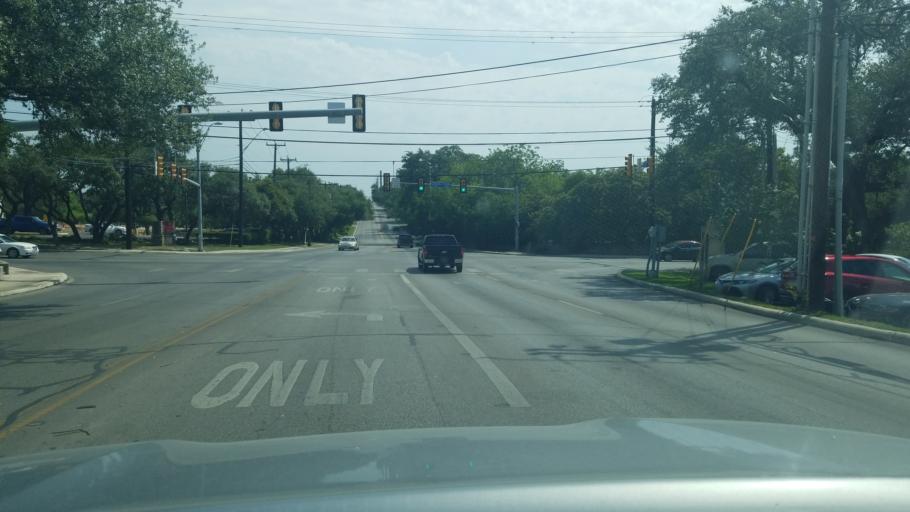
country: US
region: Texas
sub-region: Bexar County
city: Castle Hills
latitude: 29.5347
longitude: -98.5207
